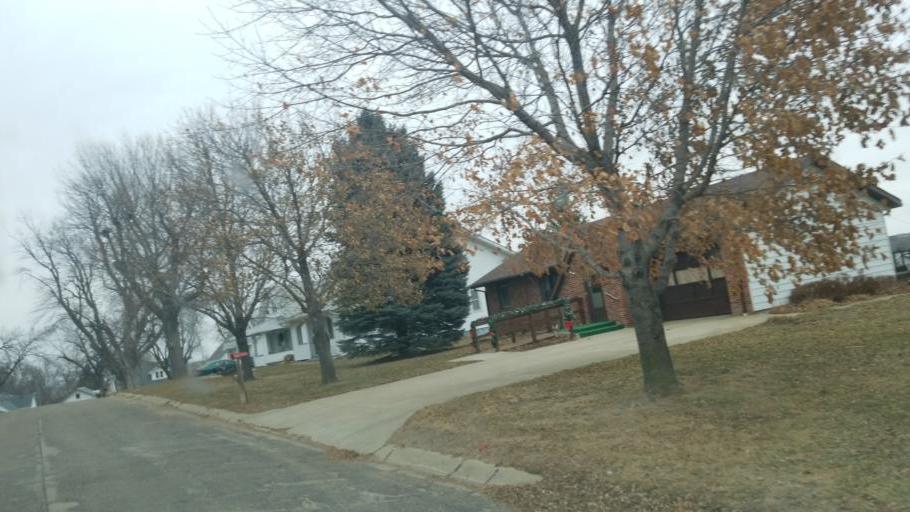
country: US
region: Nebraska
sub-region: Knox County
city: Bloomfield
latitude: 42.5966
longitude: -97.6405
